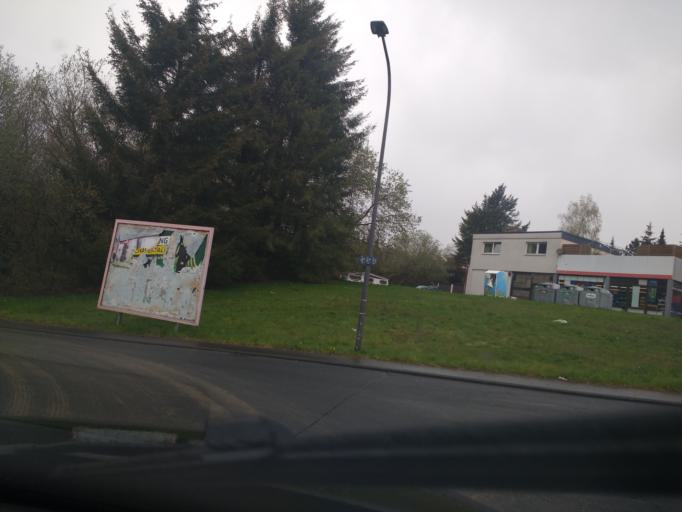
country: DE
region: Rheinland-Pfalz
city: Rommersheim
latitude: 50.2138
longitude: 6.4417
